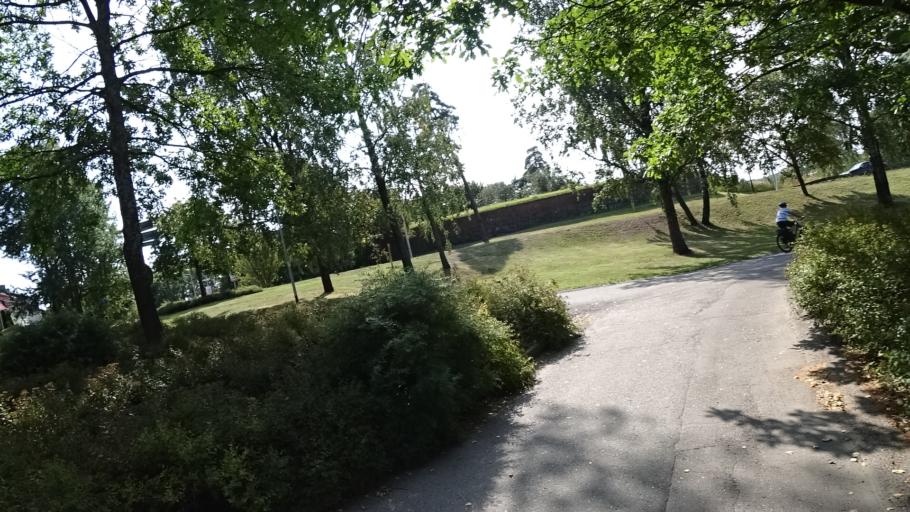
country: FI
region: Kymenlaakso
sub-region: Kotka-Hamina
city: Kotka
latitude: 60.4610
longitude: 26.9269
